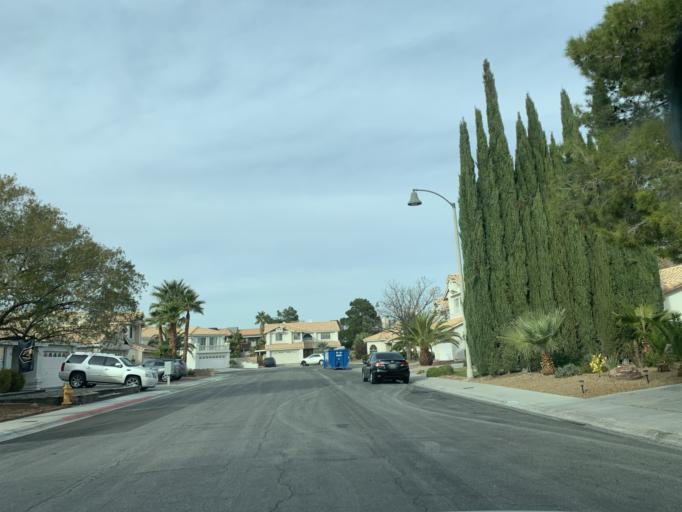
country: US
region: Nevada
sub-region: Clark County
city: Summerlin South
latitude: 36.1417
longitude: -115.2991
